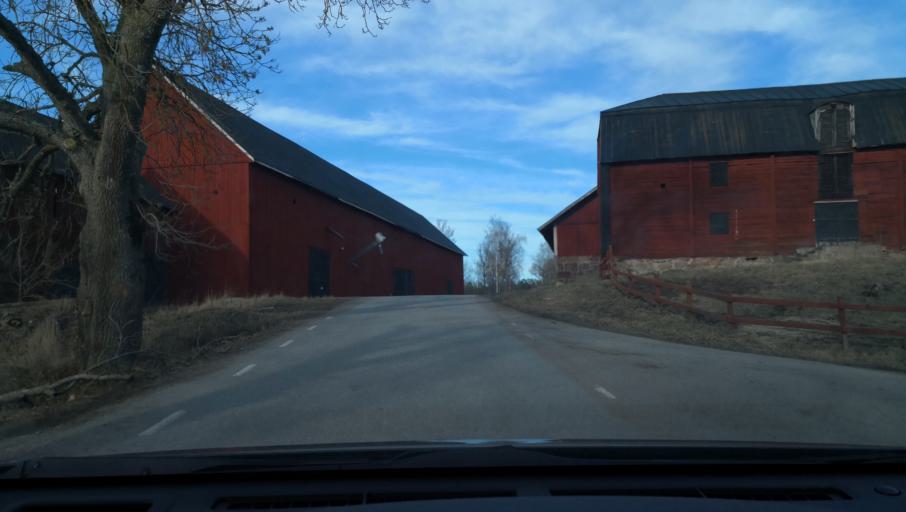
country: SE
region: Uppsala
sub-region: Enkopings Kommun
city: Grillby
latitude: 59.5433
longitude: 17.2037
